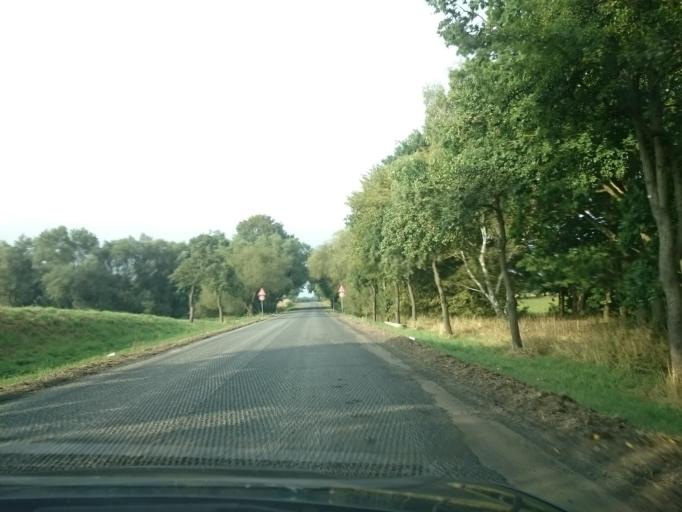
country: DE
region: Mecklenburg-Vorpommern
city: Mollenhagen
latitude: 53.6111
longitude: 12.8865
